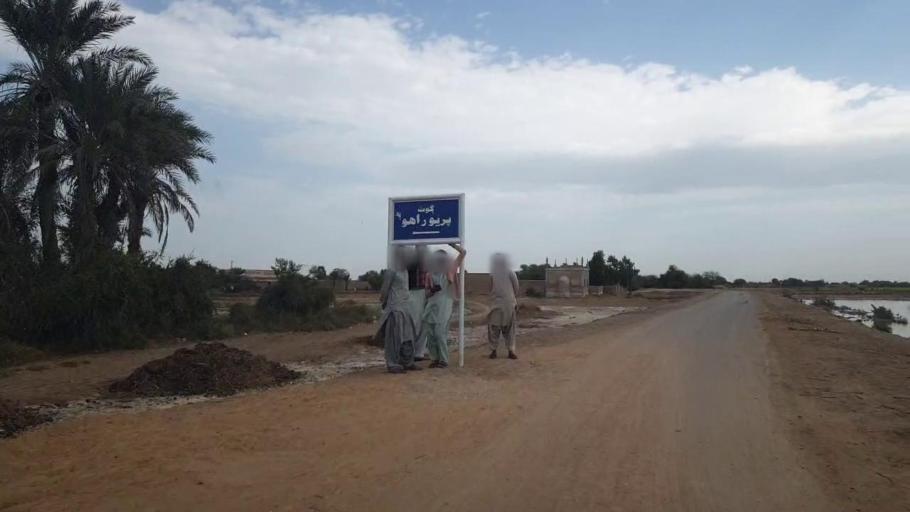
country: PK
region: Sindh
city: Hala
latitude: 25.9817
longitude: 68.4188
